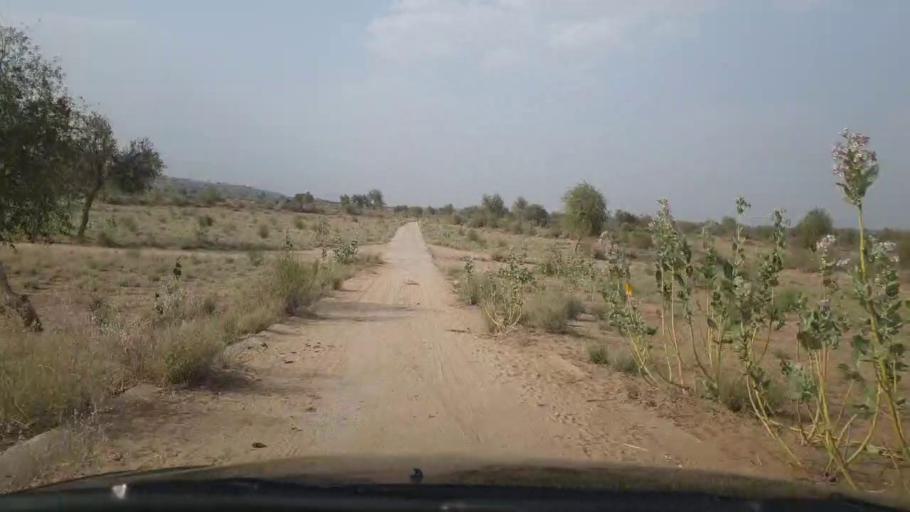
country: PK
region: Sindh
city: Islamkot
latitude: 25.0293
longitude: 70.5591
